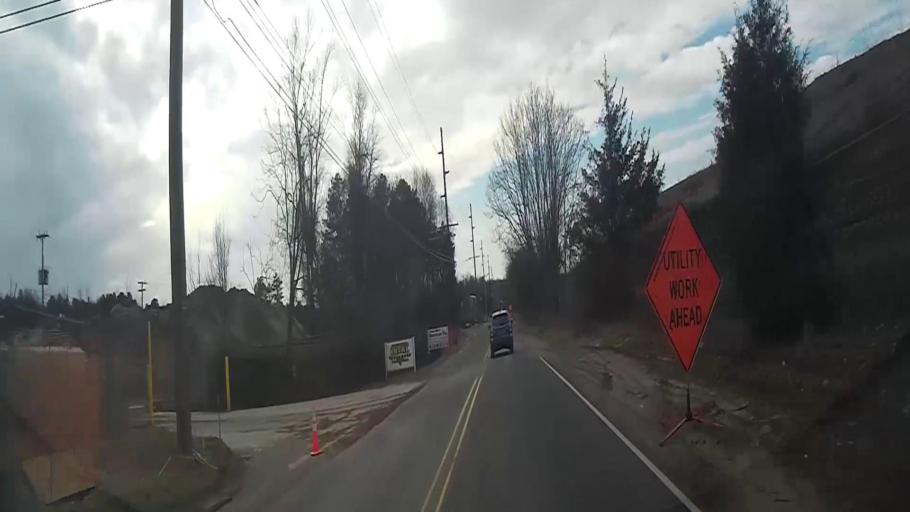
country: US
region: New Jersey
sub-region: Camden County
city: Pine Hill
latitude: 39.7786
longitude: -75.0165
